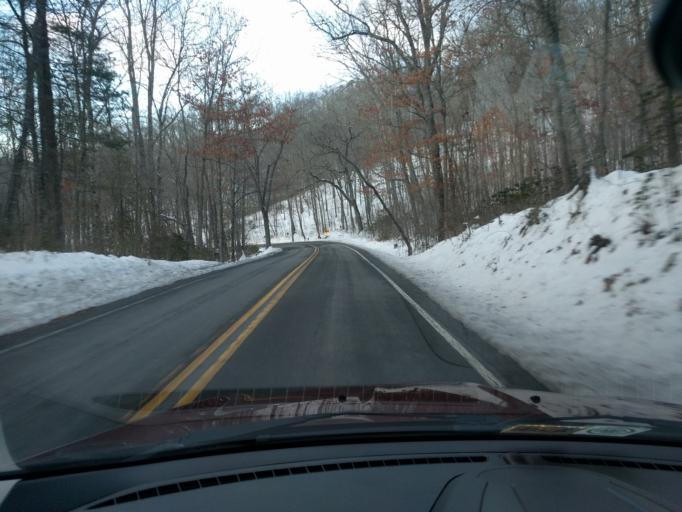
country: US
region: Virginia
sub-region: Bath County
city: Warm Springs
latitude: 38.0904
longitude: -79.8602
